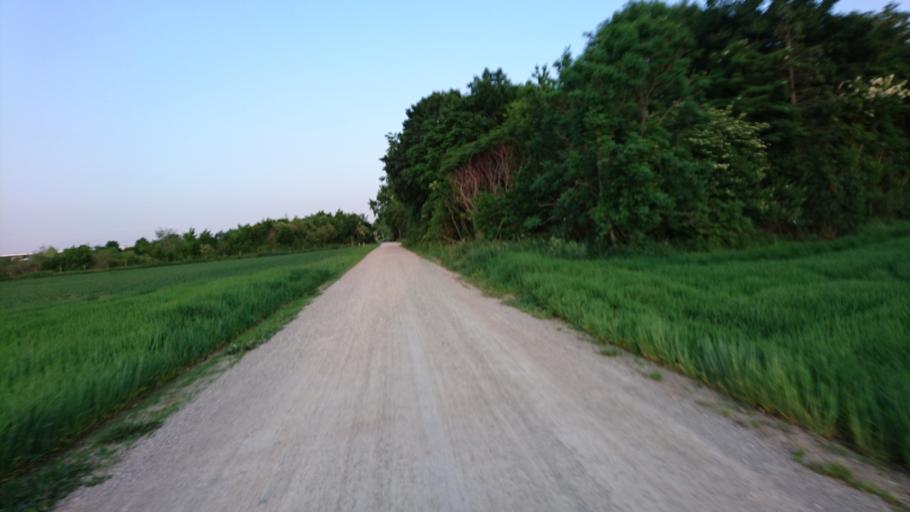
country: DE
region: Bavaria
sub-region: Upper Bavaria
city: Pliening
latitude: 48.1779
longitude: 11.7901
